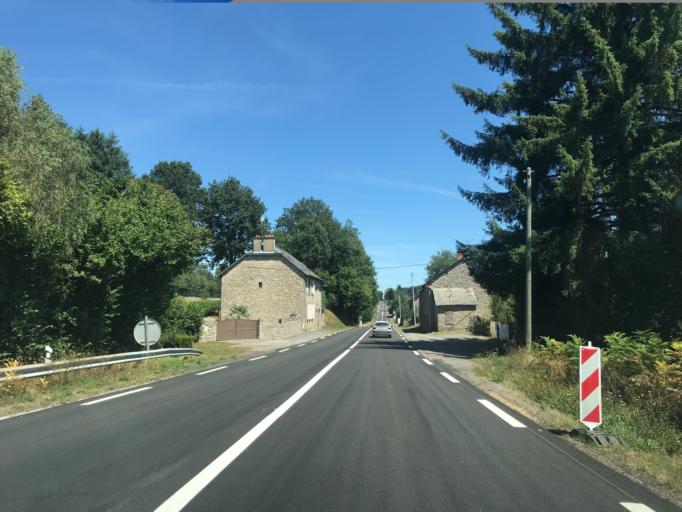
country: FR
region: Limousin
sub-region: Departement de la Correze
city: Egletons
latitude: 45.3716
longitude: 2.0022
